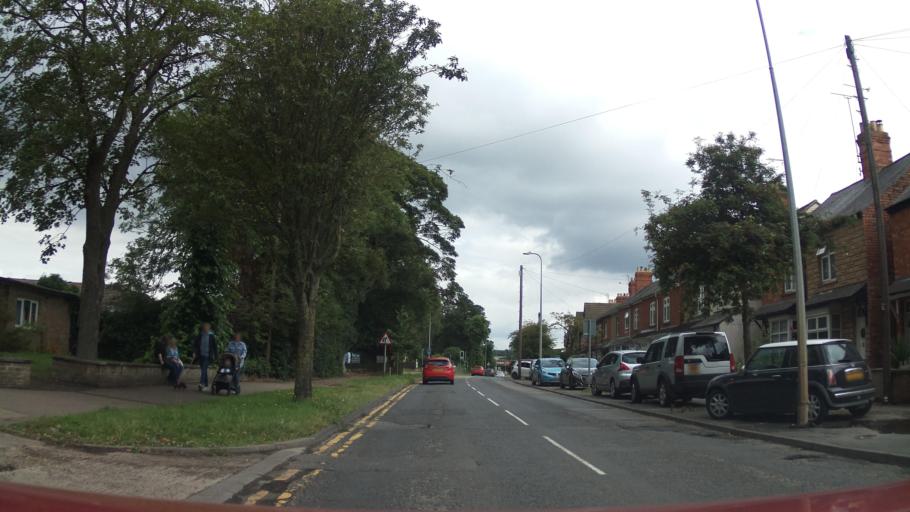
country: GB
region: England
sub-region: Lincolnshire
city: Stamford
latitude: 52.6567
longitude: -0.4681
